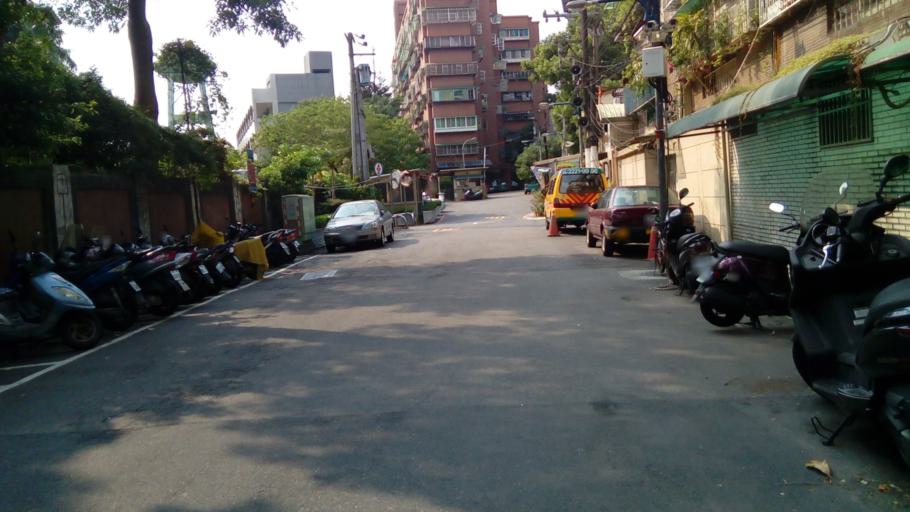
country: TW
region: Taipei
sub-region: Taipei
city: Banqiao
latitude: 25.0010
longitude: 121.4795
